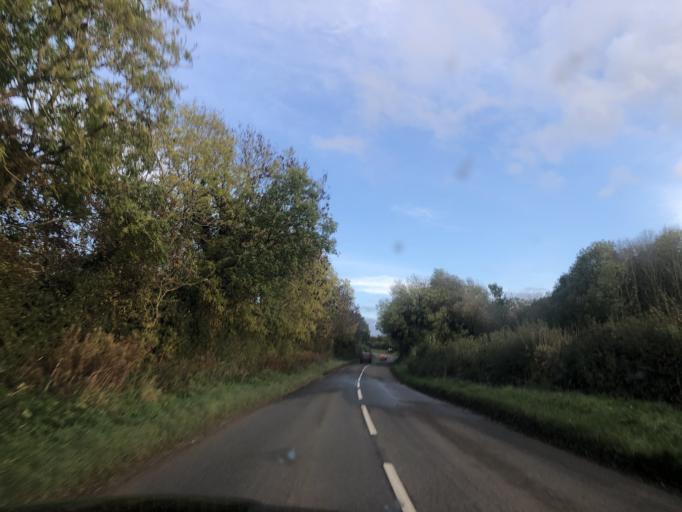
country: GB
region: England
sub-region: Warwickshire
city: Harbury
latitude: 52.2396
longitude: -1.4720
